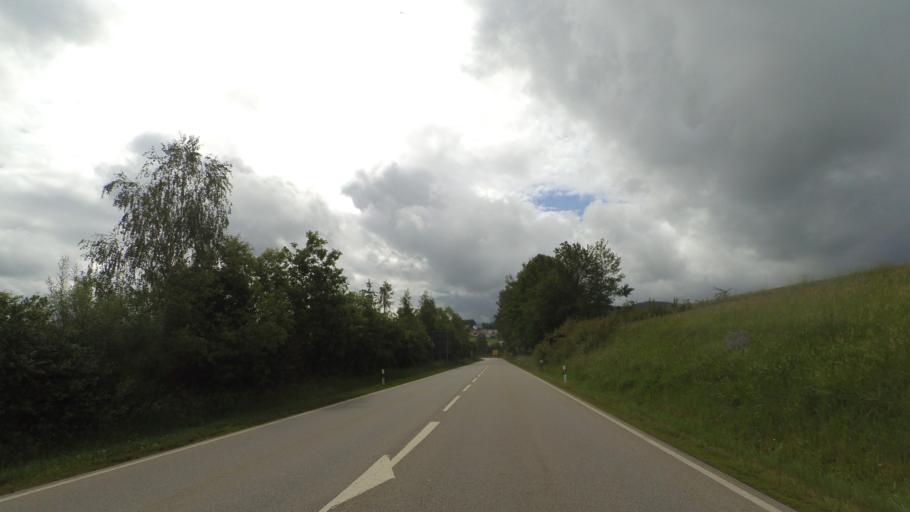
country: DE
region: Bavaria
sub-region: Lower Bavaria
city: Prackenbach
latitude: 49.0946
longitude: 12.8217
